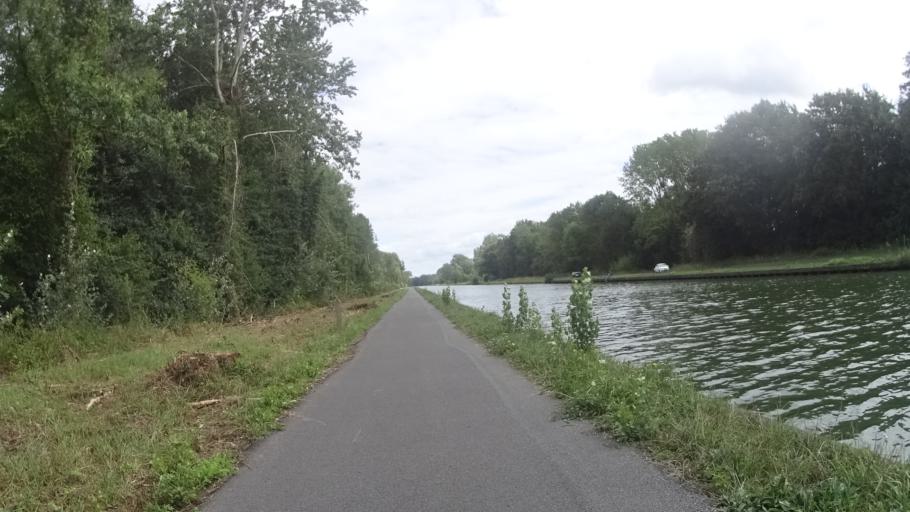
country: FR
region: Picardie
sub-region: Departement de l'Aisne
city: Ognes
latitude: 49.5799
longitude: 3.1436
